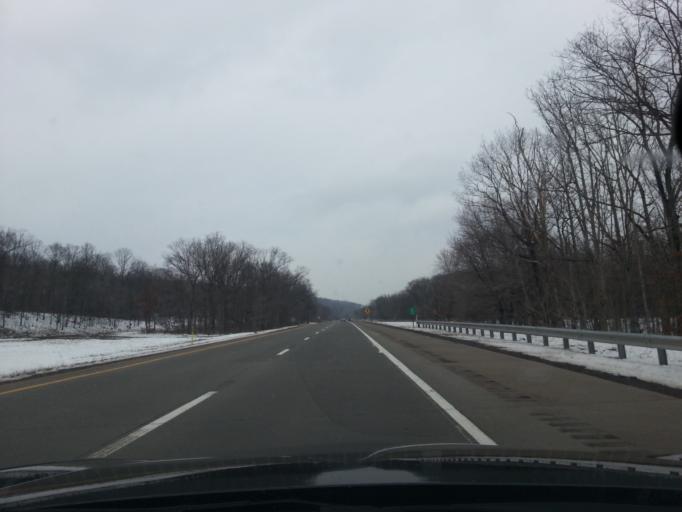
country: US
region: Pennsylvania
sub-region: Luzerne County
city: Conyngham
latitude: 41.0497
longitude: -76.0099
